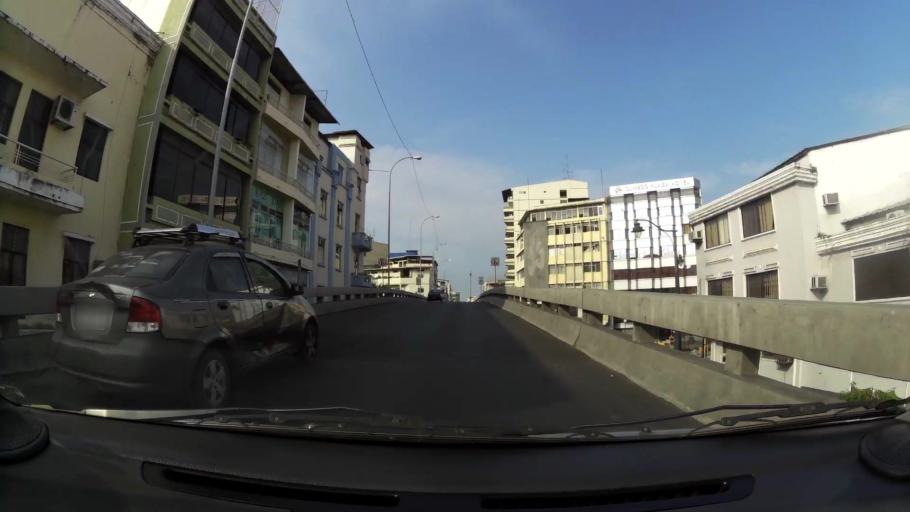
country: EC
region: Guayas
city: Guayaquil
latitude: -2.1986
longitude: -79.8836
